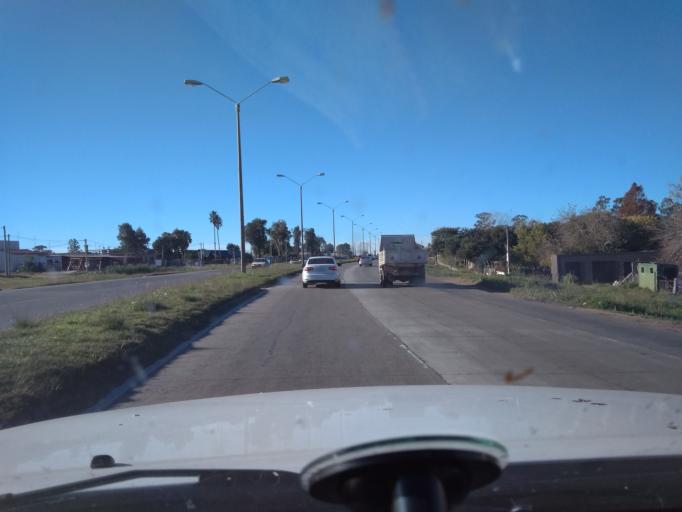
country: UY
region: Canelones
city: Colonia Nicolich
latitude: -34.7809
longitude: -56.0596
